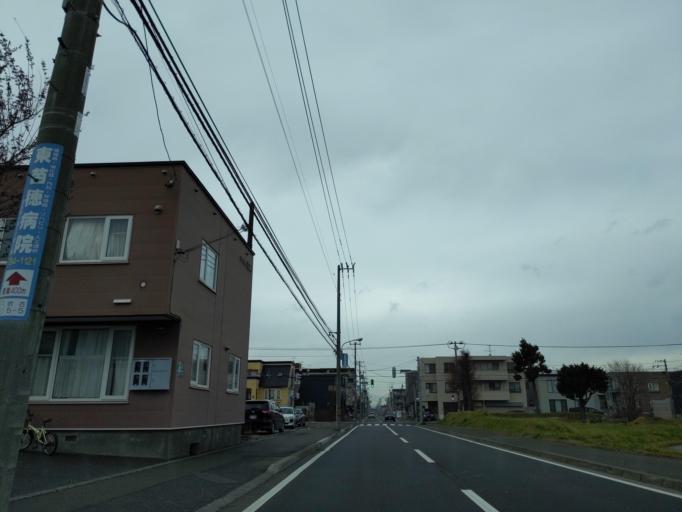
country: JP
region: Hokkaido
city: Sapporo
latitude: 43.0858
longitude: 141.3967
